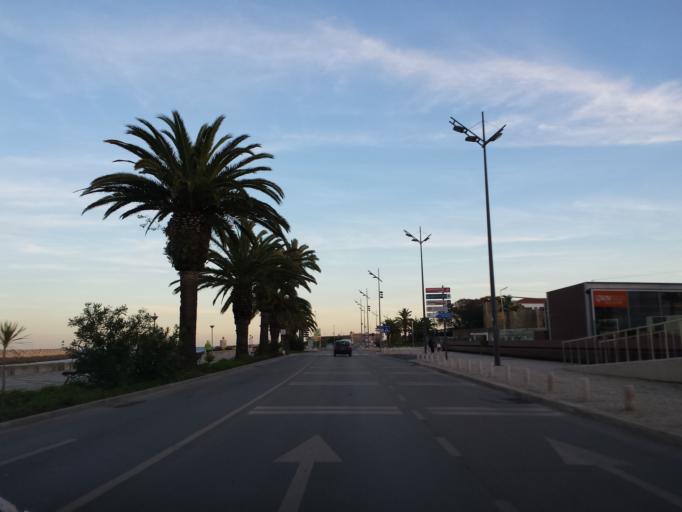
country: PT
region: Faro
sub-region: Lagos
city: Lagos
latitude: 37.1016
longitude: -8.6707
